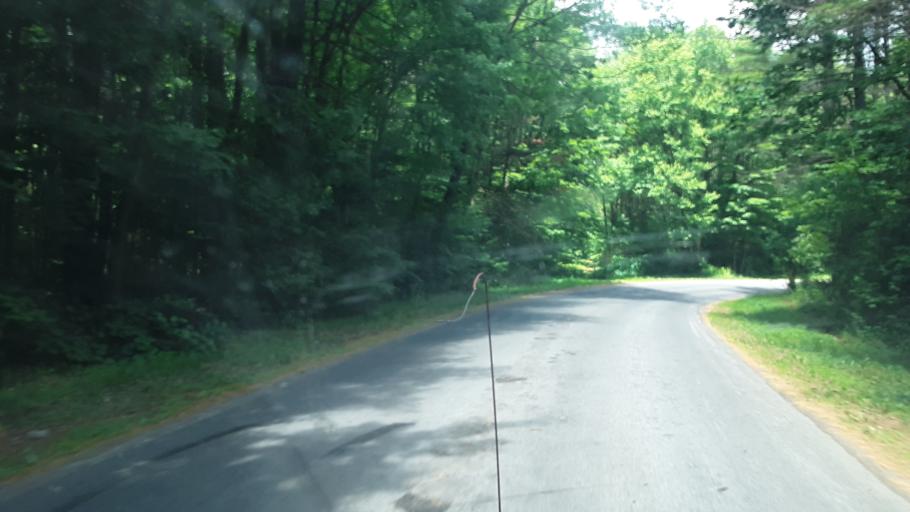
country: US
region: New York
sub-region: Oneida County
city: Rome
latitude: 43.2571
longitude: -75.5962
